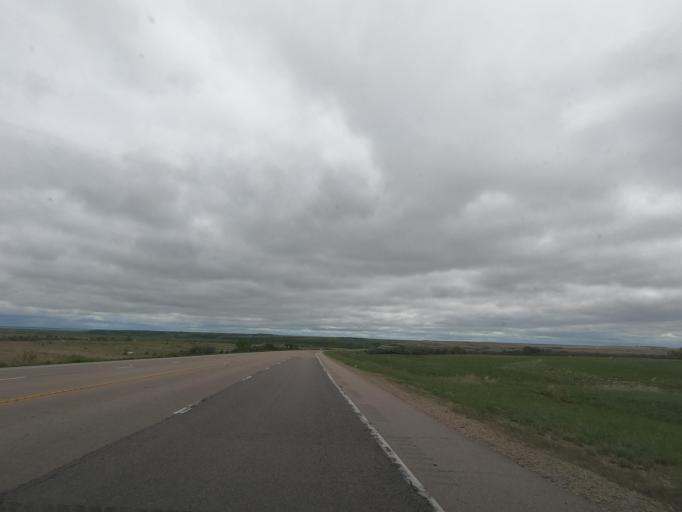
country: US
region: Kansas
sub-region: Greenwood County
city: Eureka
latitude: 37.6614
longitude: -96.4977
